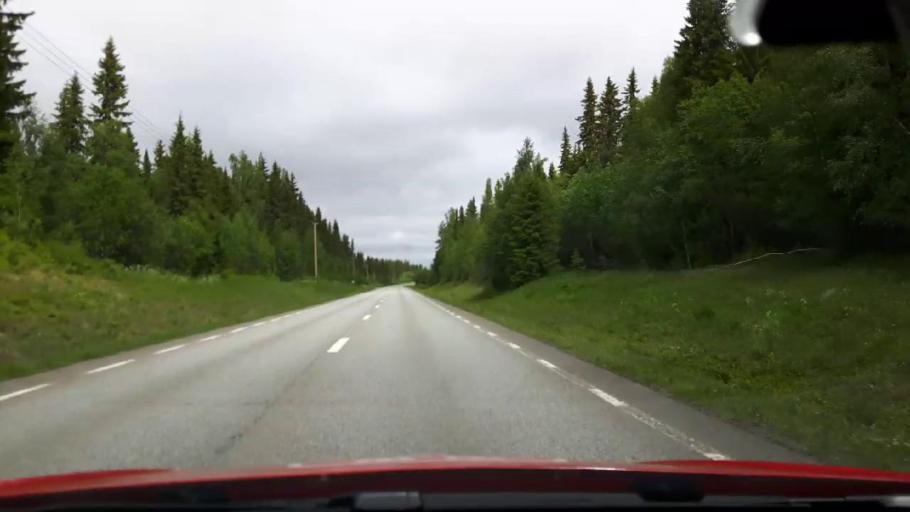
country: SE
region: Jaemtland
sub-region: Krokoms Kommun
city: Krokom
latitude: 63.4891
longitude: 14.5061
